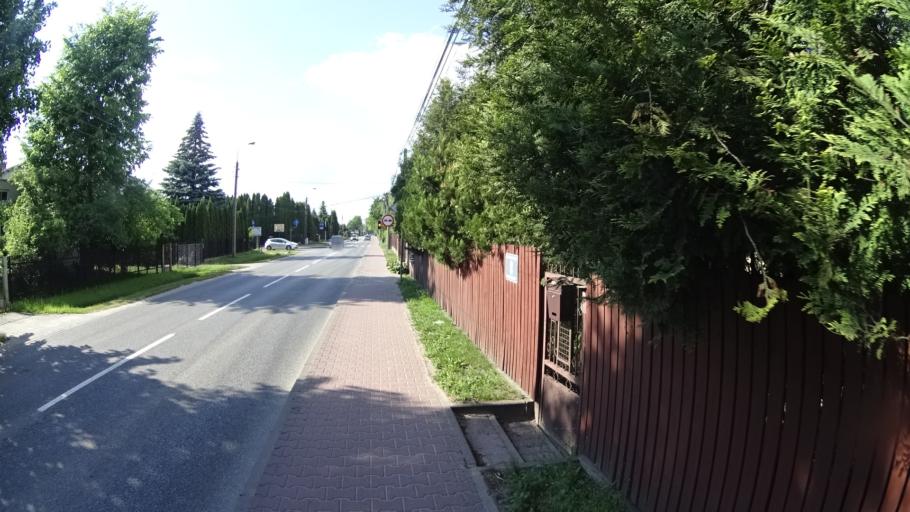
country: PL
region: Masovian Voivodeship
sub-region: Powiat pruszkowski
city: Nadarzyn
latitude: 52.0965
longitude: 20.8070
